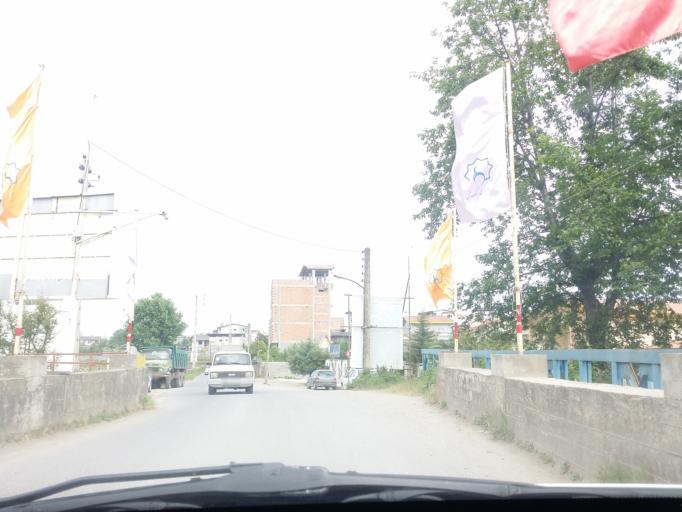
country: IR
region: Mazandaran
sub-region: Nowshahr
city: Nowshahr
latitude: 36.6252
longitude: 51.4913
